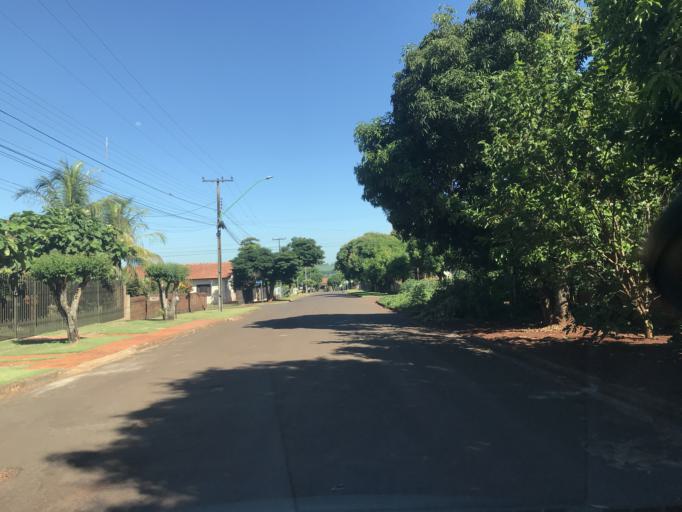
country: BR
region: Parana
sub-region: Palotina
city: Palotina
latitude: -24.2742
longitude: -53.8434
